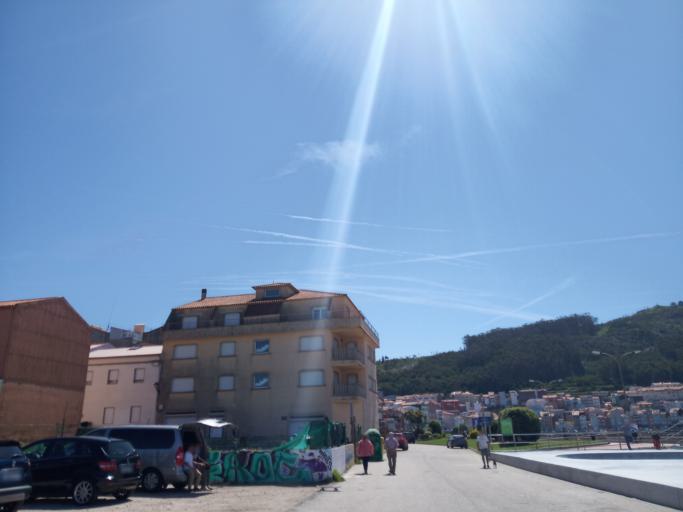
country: ES
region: Galicia
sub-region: Provincia de Pontevedra
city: A Guarda
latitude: 41.9022
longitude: -8.8793
